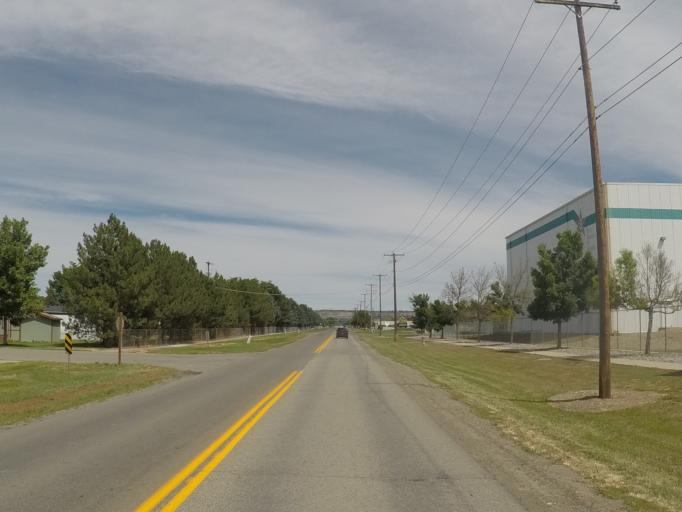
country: US
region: Montana
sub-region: Yellowstone County
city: Billings
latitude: 45.7502
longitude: -108.5968
